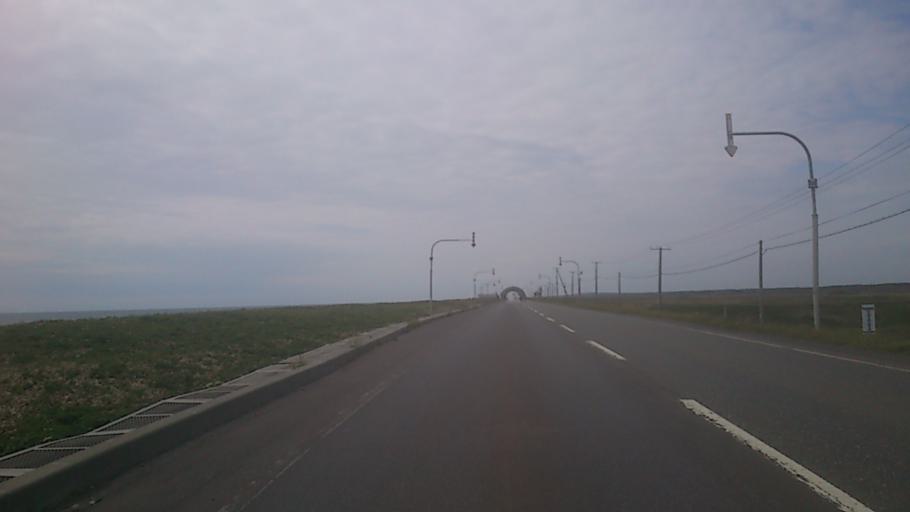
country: JP
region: Hokkaido
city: Makubetsu
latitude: 44.9999
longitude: 141.6827
